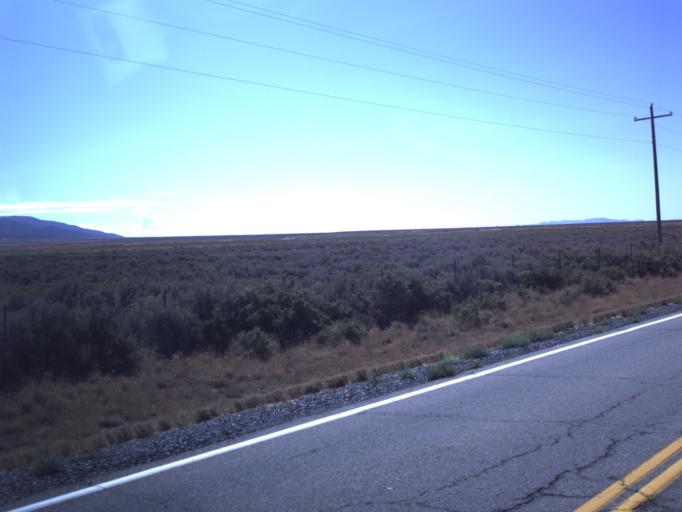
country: US
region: Utah
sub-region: Tooele County
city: Tooele
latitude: 40.3921
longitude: -112.3862
